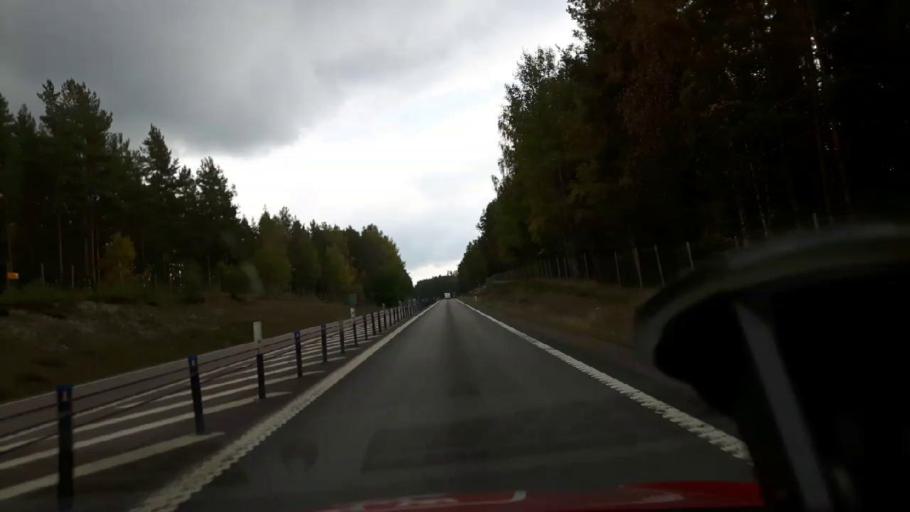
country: SE
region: Gaevleborg
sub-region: Gavle Kommun
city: Norrsundet
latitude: 61.0011
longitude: 16.9908
